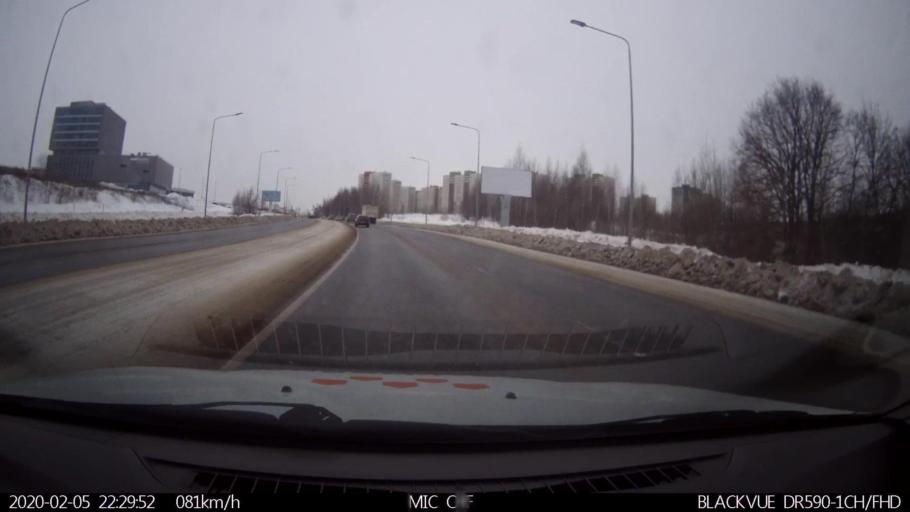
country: RU
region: Nizjnij Novgorod
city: Imeni Stepana Razina
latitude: 54.7464
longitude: 44.1500
